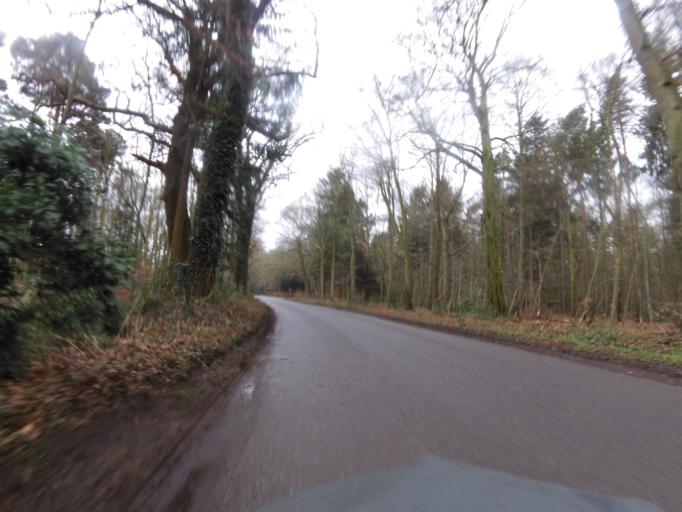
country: GB
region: England
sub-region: Norfolk
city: Briston
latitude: 52.8652
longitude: 1.0700
